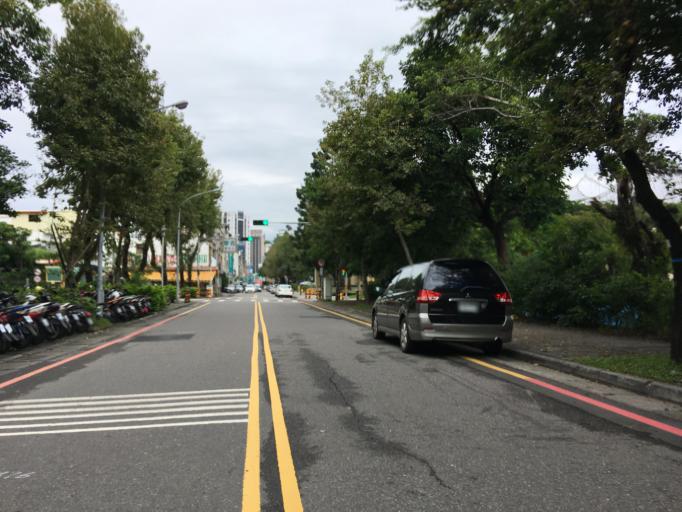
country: TW
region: Taiwan
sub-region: Yilan
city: Yilan
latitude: 24.7478
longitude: 121.7459
